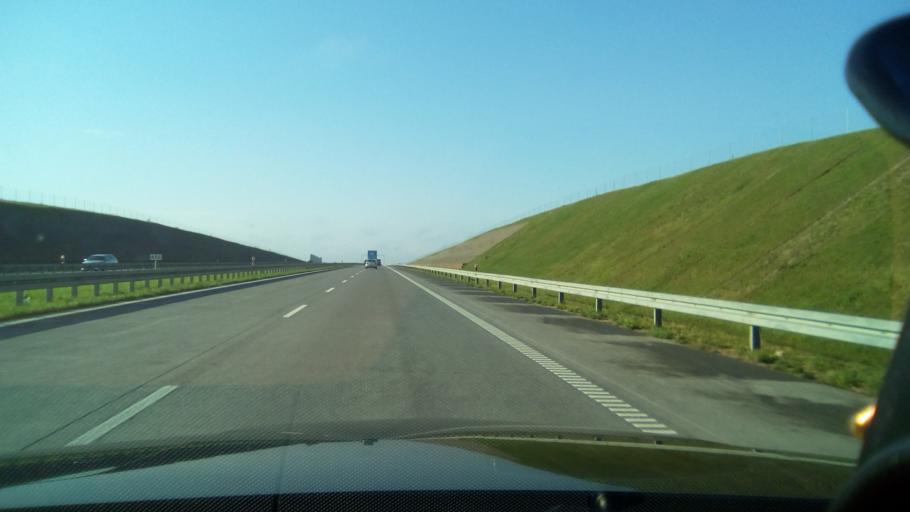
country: PL
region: Silesian Voivodeship
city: Wozniki
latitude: 50.6215
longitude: 19.0319
